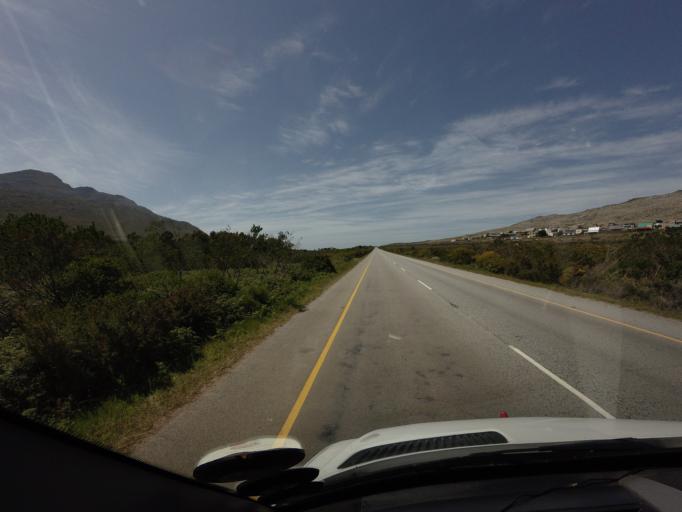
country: ZA
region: Western Cape
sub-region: Overberg District Municipality
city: Grabouw
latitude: -34.3404
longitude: 18.8444
